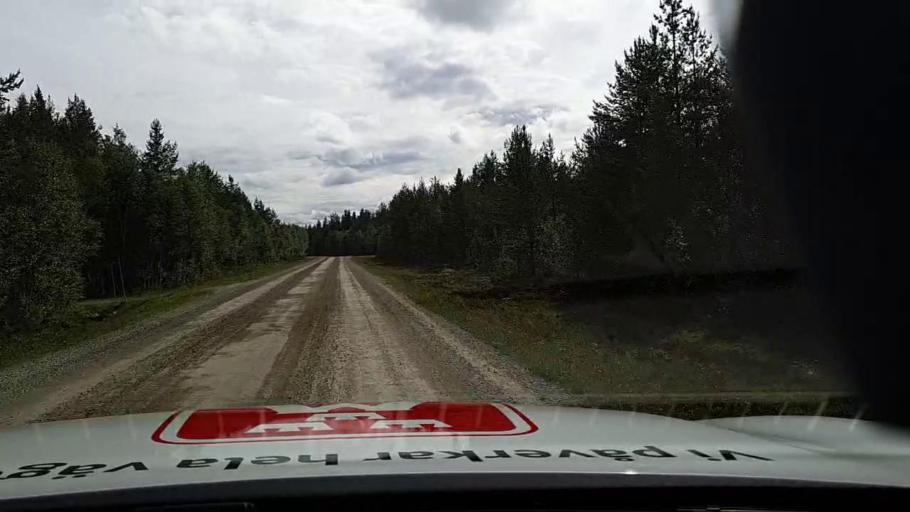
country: SE
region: Jaemtland
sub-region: Are Kommun
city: Jarpen
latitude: 62.5229
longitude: 13.4885
